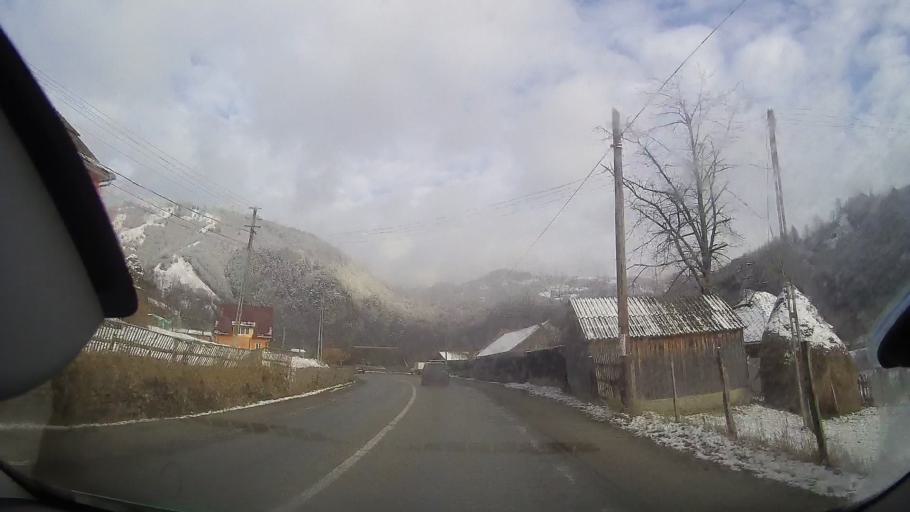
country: RO
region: Alba
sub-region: Oras Baia de Aries
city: Baia de Aries
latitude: 46.3949
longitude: 23.2999
